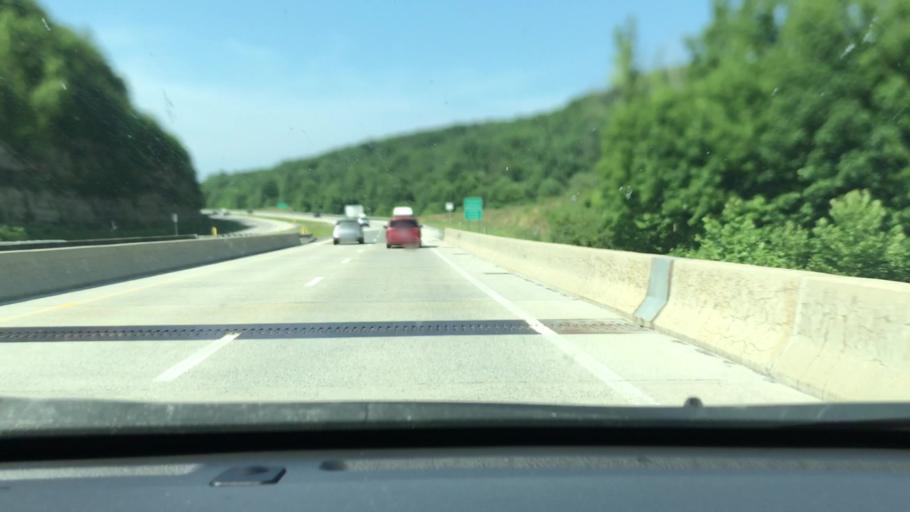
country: US
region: West Virginia
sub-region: Nicholas County
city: Summersville
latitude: 38.1502
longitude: -80.9289
